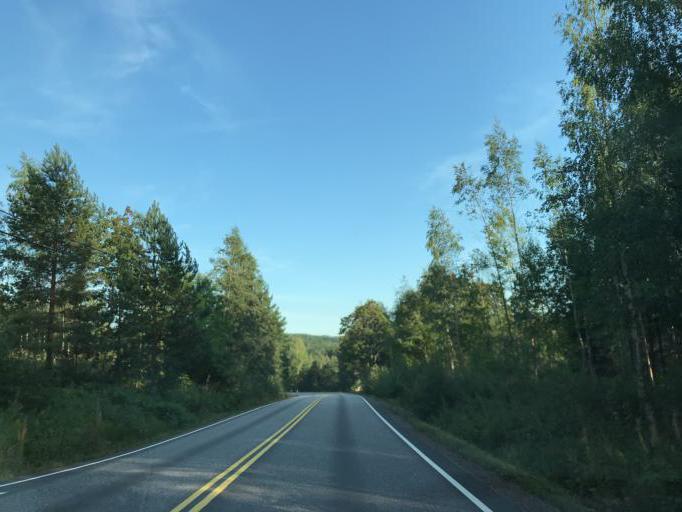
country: FI
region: Uusimaa
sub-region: Helsinki
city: Vihti
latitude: 60.4177
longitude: 24.3890
